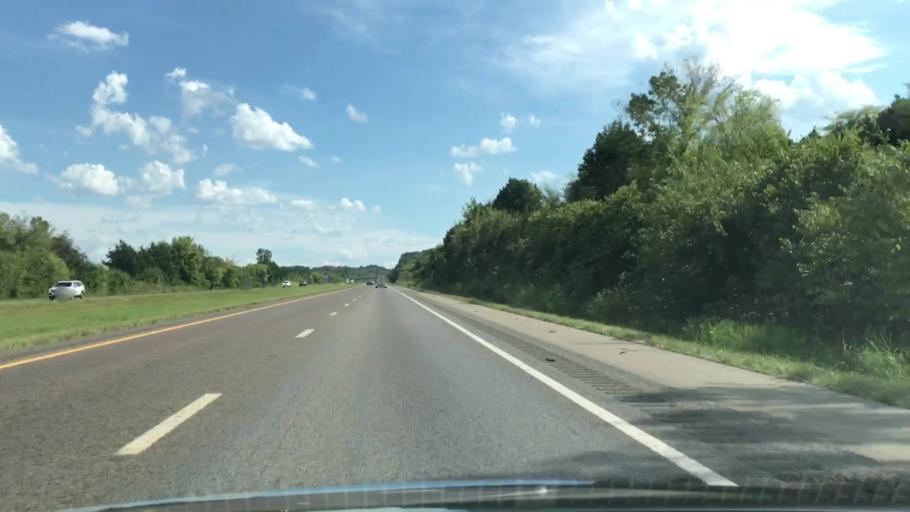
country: US
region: Tennessee
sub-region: Marshall County
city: Lewisburg
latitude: 35.5068
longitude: -86.8944
